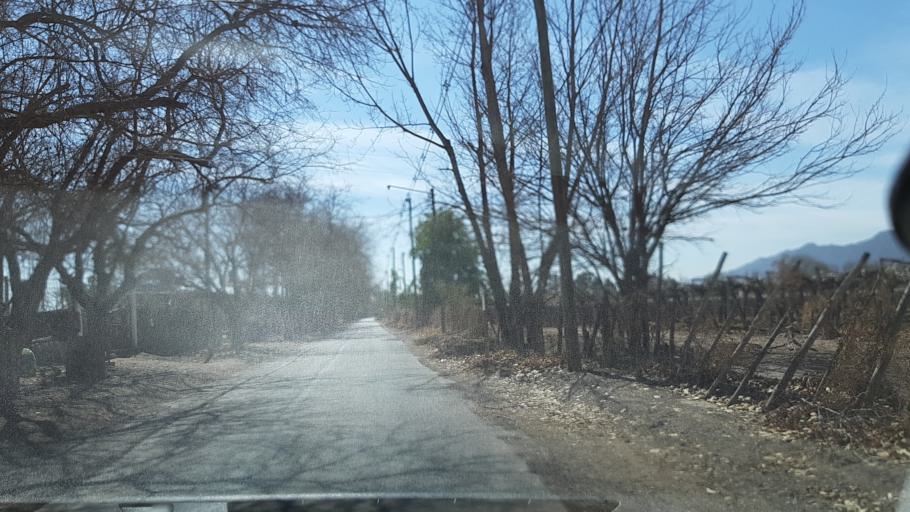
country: AR
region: San Juan
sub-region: Departamento de Zonda
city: Zonda
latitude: -31.5651
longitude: -68.7302
